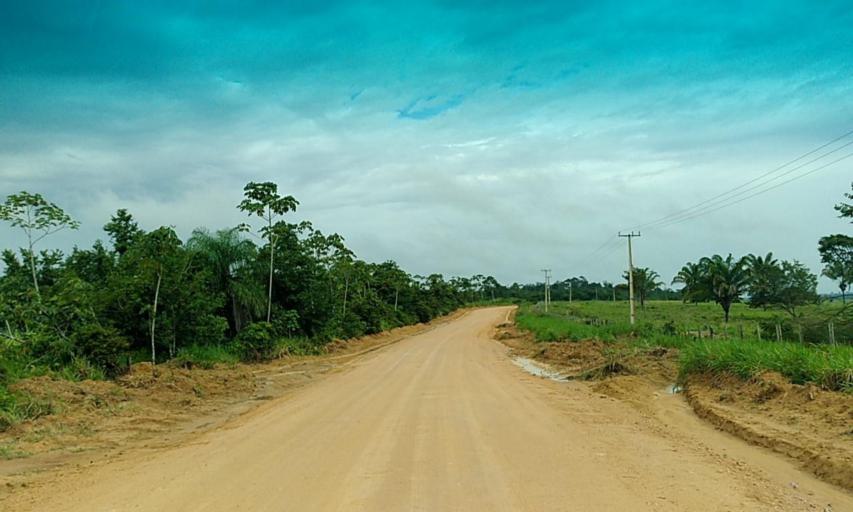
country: BR
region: Para
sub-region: Senador Jose Porfirio
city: Senador Jose Porfirio
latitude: -3.0572
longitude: -51.6770
